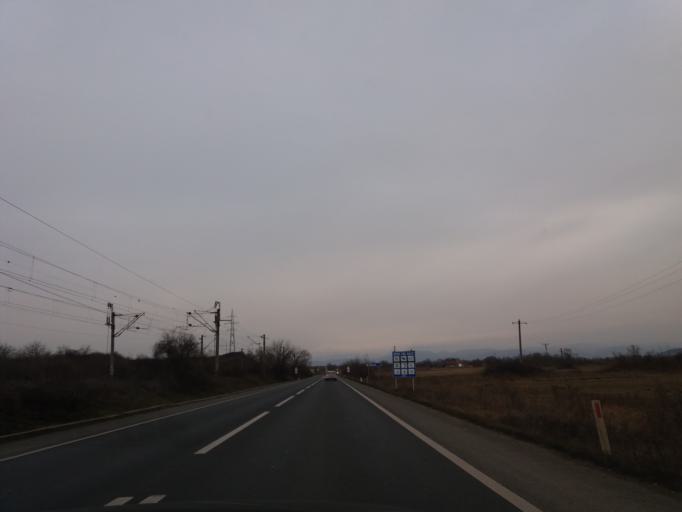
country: RO
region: Hunedoara
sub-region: Comuna Calan
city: Calan
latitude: 45.7658
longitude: 23.0001
